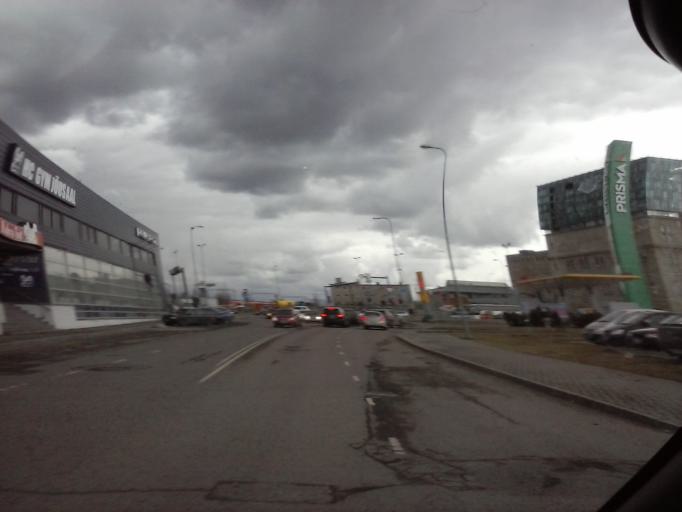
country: EE
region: Harju
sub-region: Tallinna linn
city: Tallinn
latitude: 59.4255
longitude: 24.7856
